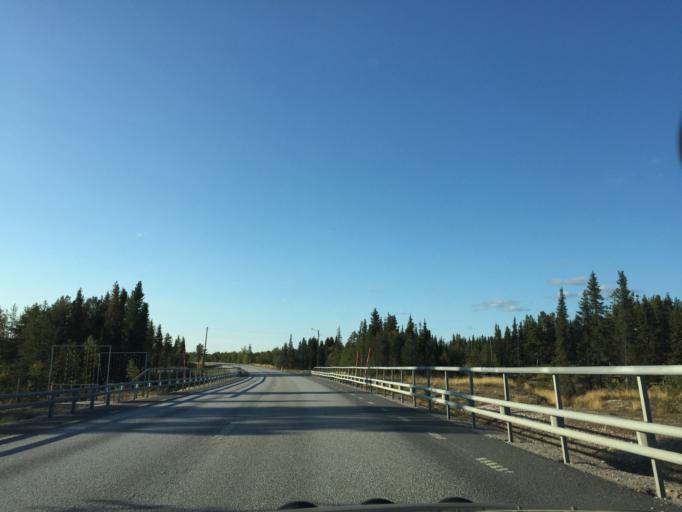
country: SE
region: Norrbotten
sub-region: Gallivare Kommun
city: Malmberget
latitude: 67.6394
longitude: 21.0622
